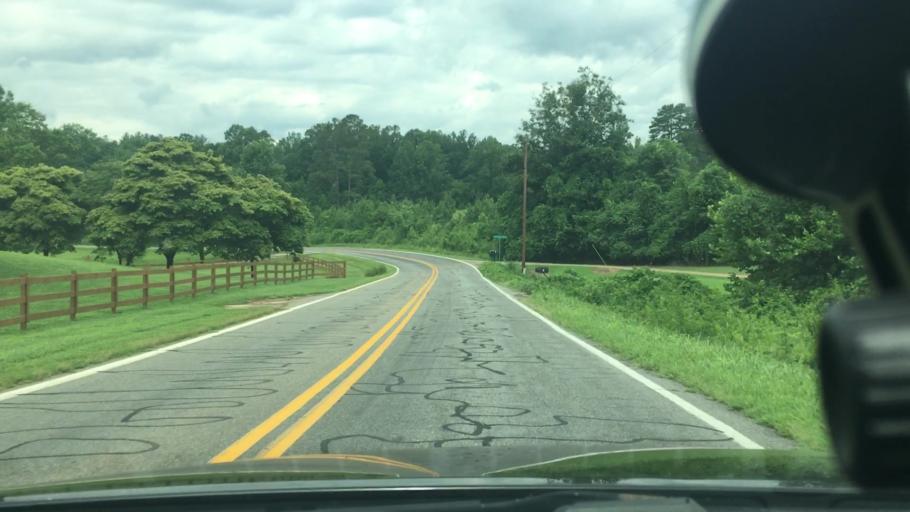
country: US
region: North Carolina
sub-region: Rutherford County
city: Rutherfordton
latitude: 35.3782
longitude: -81.9803
